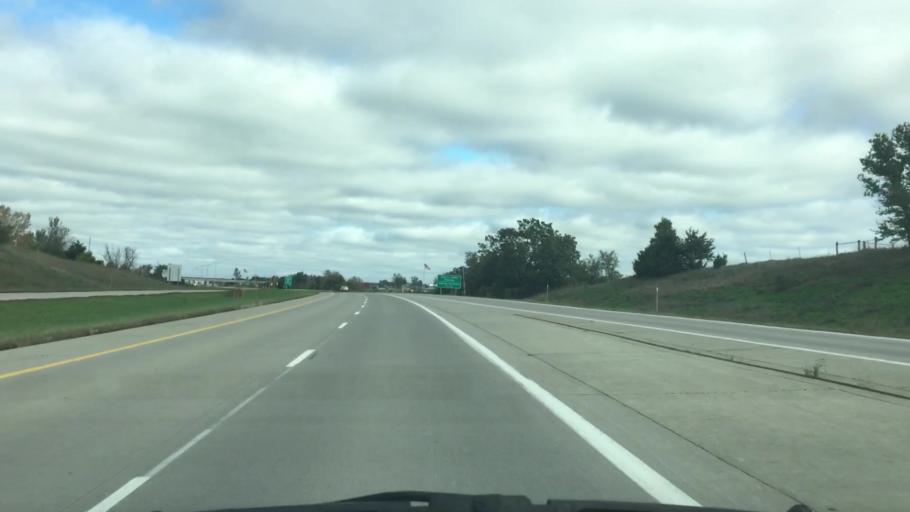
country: US
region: Iowa
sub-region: Clarke County
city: Osceola
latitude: 41.0173
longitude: -93.7946
